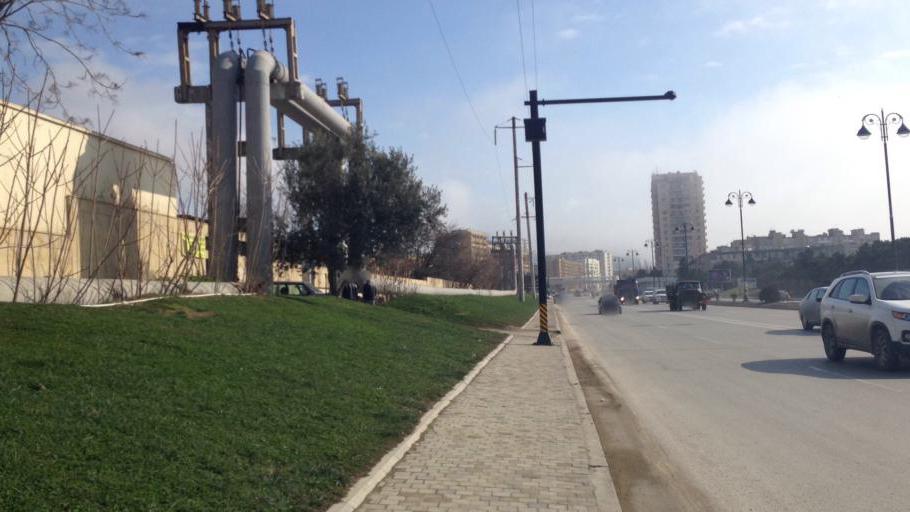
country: AZ
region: Baki
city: Baku
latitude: 40.3695
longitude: 49.9349
